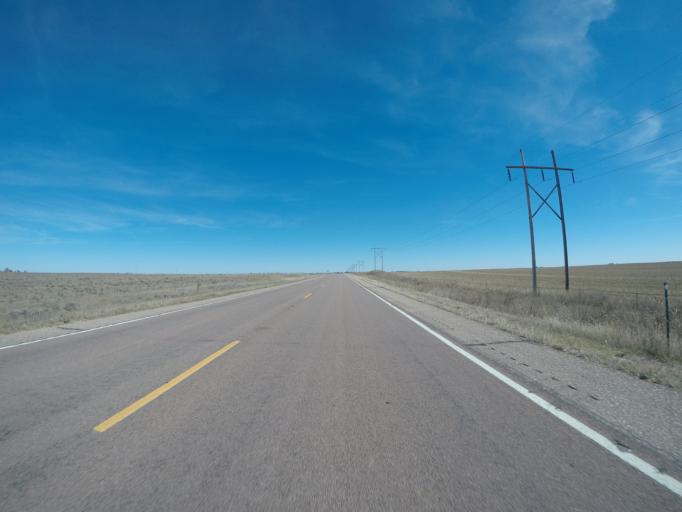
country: US
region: Colorado
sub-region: Yuma County
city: Yuma
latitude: 39.6557
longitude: -102.7316
